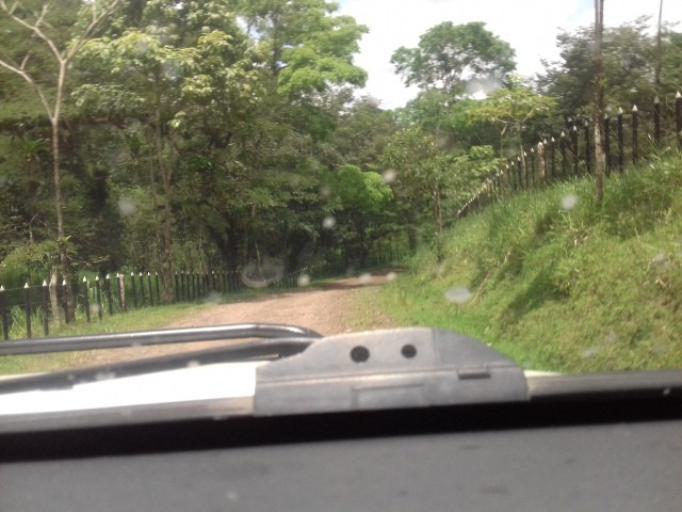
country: NI
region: Matagalpa
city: Rio Blanco
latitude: 12.9848
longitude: -85.3781
